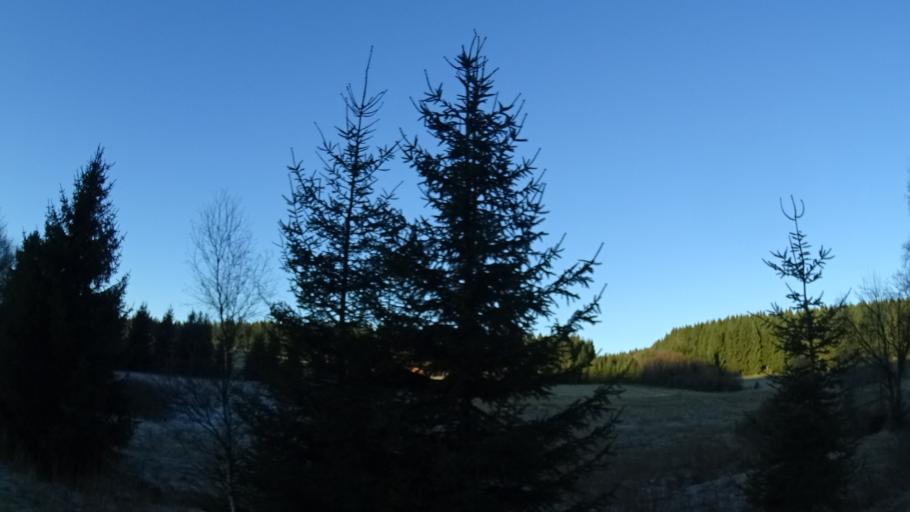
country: DE
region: Bavaria
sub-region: Upper Franconia
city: Tettau
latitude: 50.4808
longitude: 11.2646
